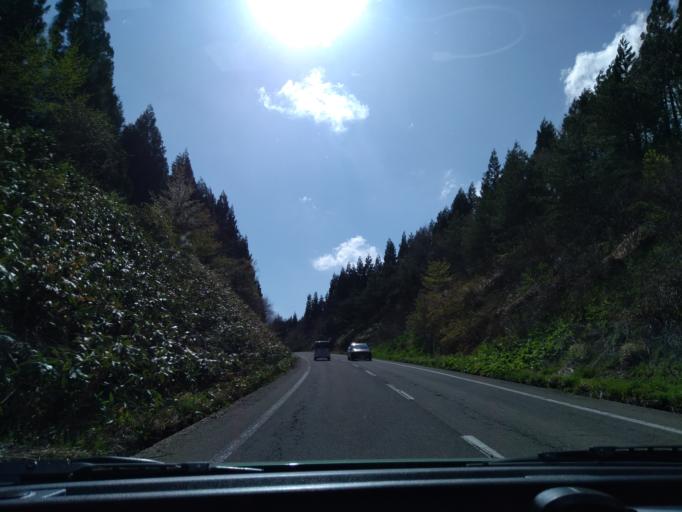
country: JP
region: Akita
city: Akita
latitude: 39.6969
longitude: 140.2538
